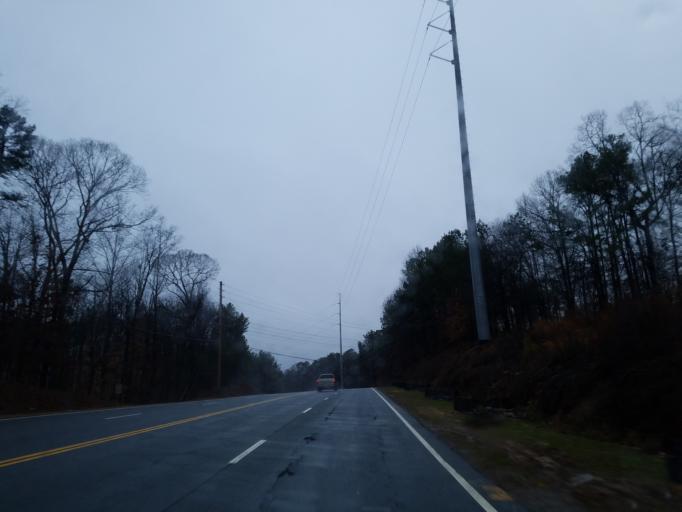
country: US
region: Georgia
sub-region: Gwinnett County
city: Norcross
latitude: 33.9815
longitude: -84.2672
